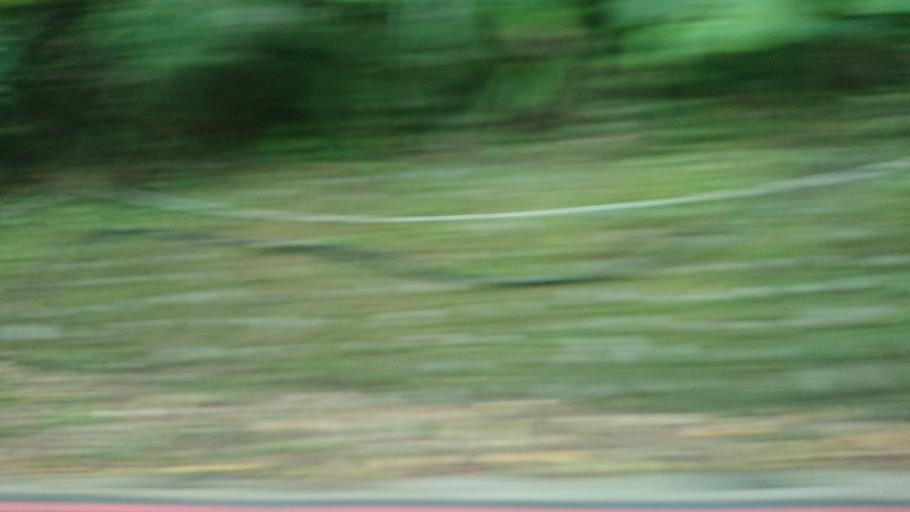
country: TW
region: Taiwan
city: Daxi
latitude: 24.8733
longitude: 121.3870
